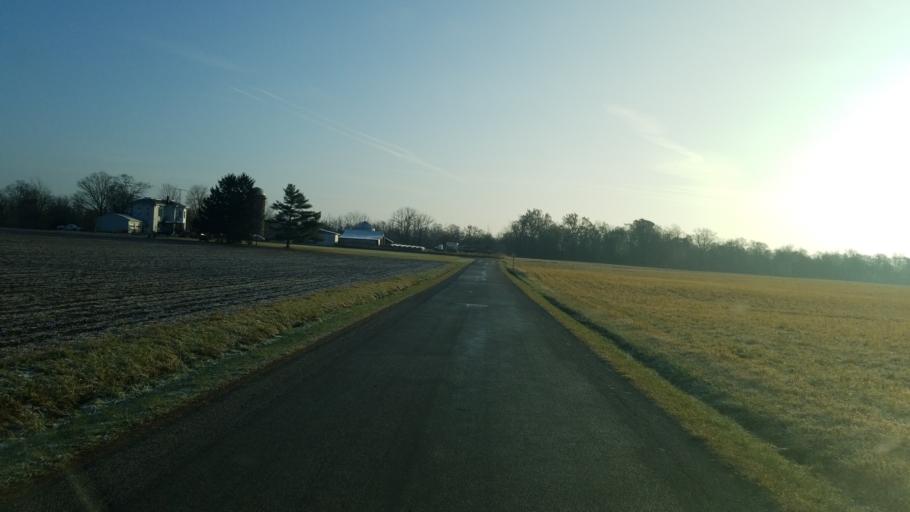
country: US
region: Ohio
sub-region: Crawford County
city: Bucyrus
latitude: 40.7576
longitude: -82.9040
